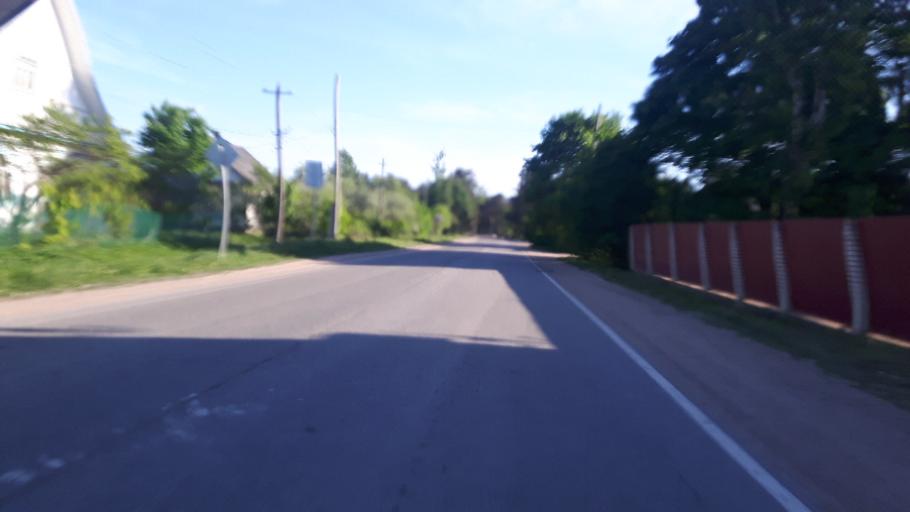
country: RU
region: Leningrad
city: Vistino
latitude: 59.7746
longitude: 28.4767
